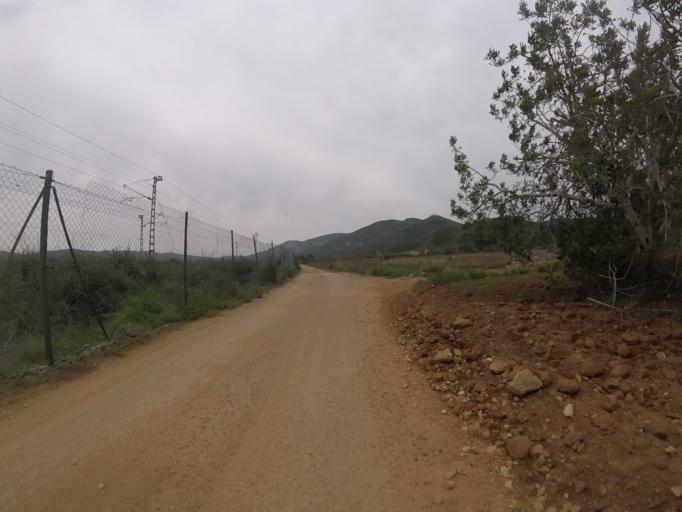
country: ES
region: Valencia
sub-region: Provincia de Castello
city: Alcoceber
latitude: 40.2535
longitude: 0.2506
